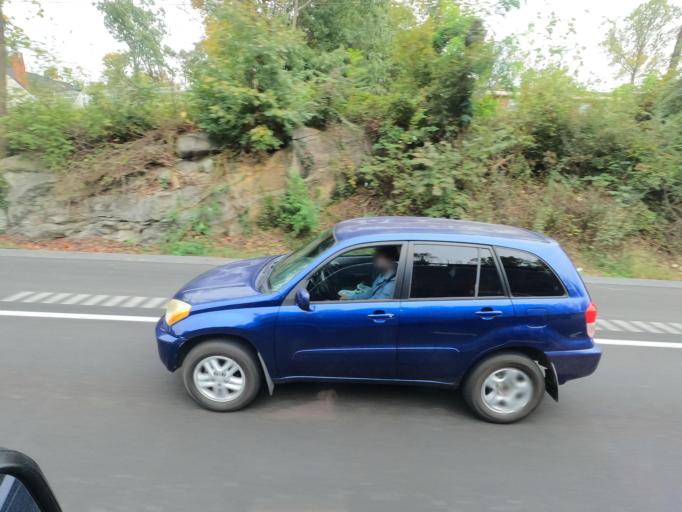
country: US
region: Tennessee
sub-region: Sullivan County
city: Colonial Heights
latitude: 36.5174
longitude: -82.5236
